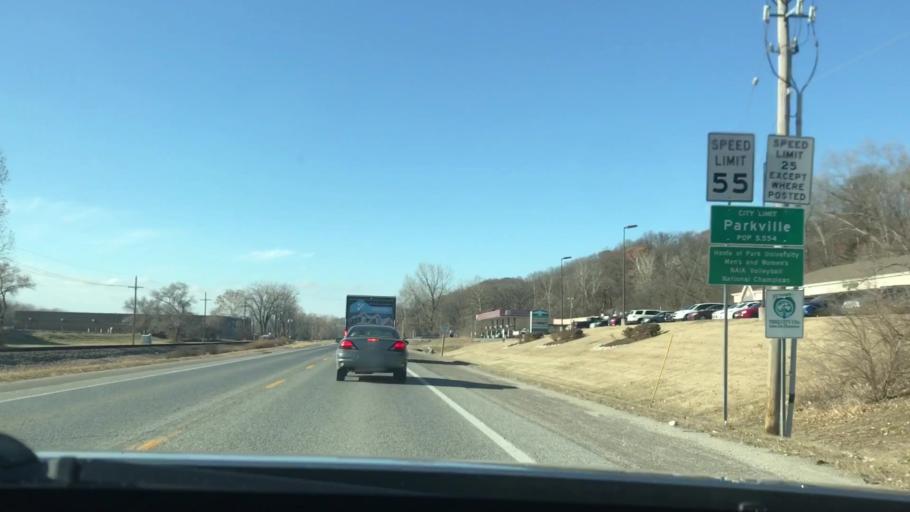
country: US
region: Missouri
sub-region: Platte County
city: Parkville
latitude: 39.1806
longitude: -94.6601
